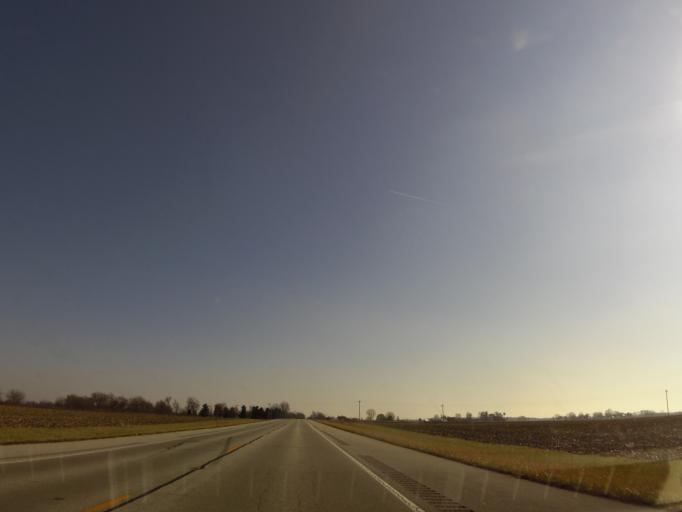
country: US
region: Indiana
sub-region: Union County
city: Liberty
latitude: 39.6056
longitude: -84.8781
